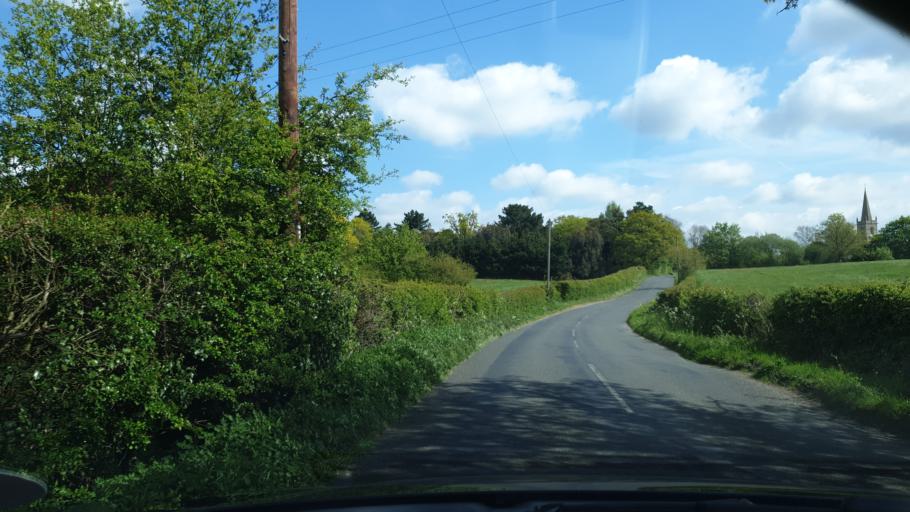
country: GB
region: England
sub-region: Essex
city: Great Bentley
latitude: 51.8733
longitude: 1.1083
